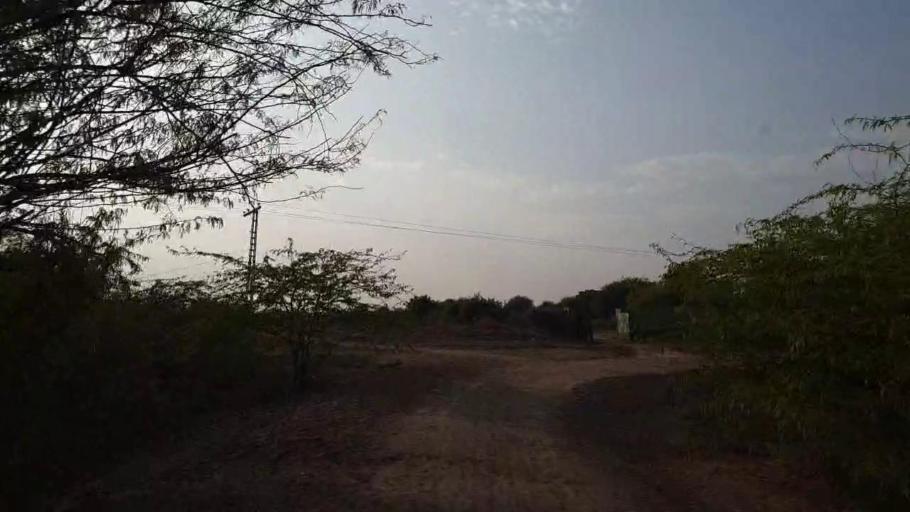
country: PK
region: Sindh
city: Pithoro
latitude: 25.5737
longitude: 69.3622
